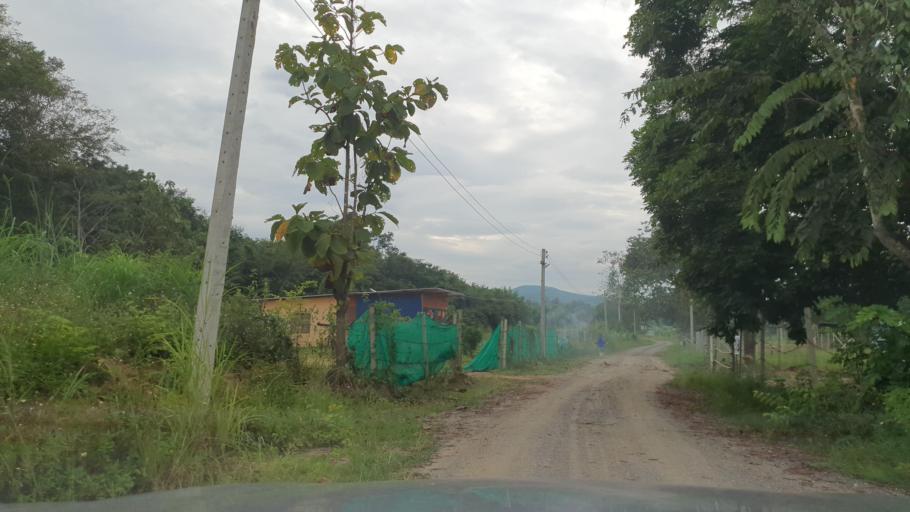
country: TH
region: Chiang Mai
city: San Sai
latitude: 18.9440
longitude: 98.9071
